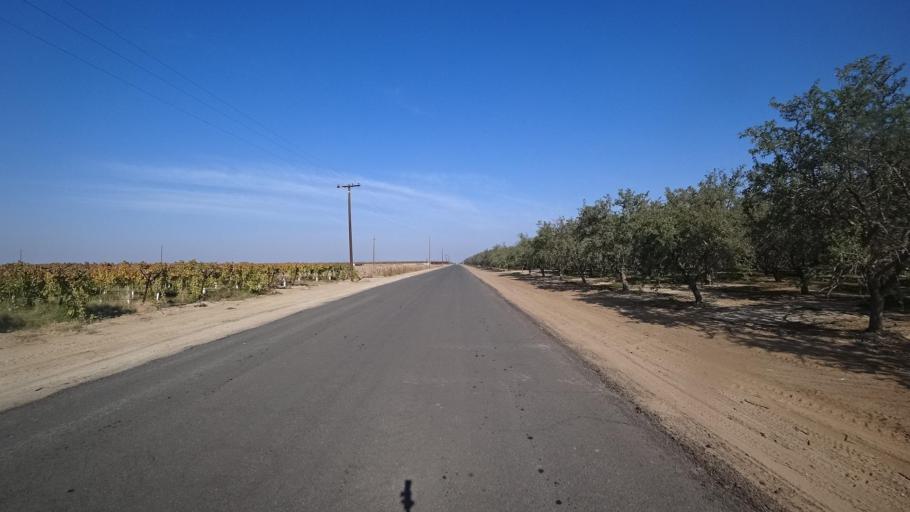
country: US
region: California
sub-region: Kern County
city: McFarland
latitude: 35.6487
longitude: -119.1868
